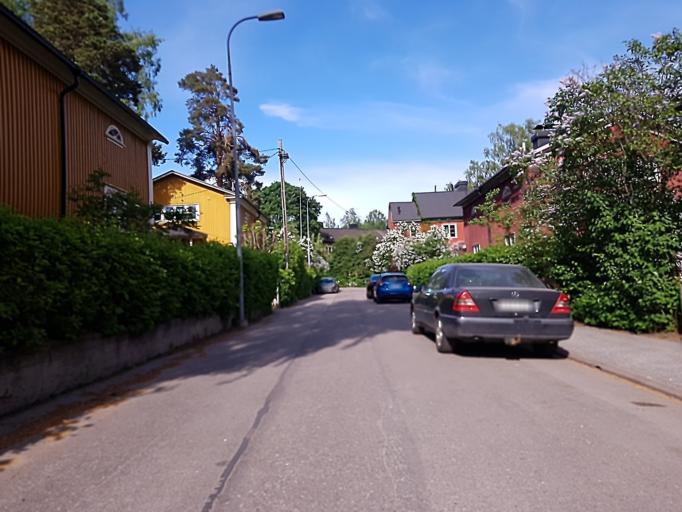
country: FI
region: Uusimaa
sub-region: Helsinki
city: Helsinki
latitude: 60.2168
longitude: 24.9503
